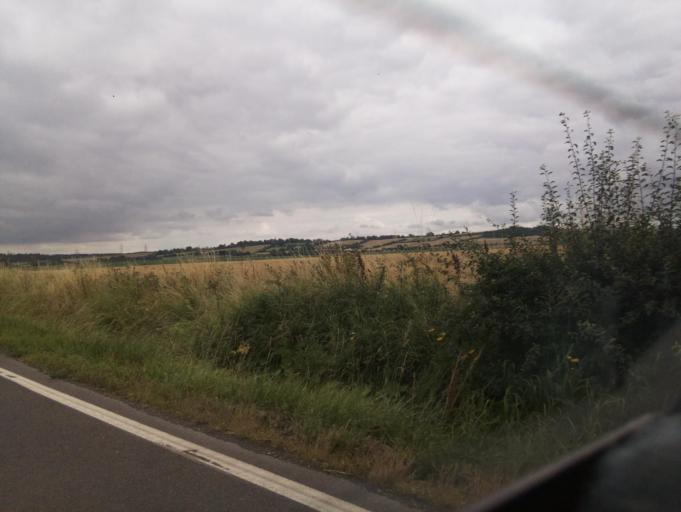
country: GB
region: England
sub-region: Lincolnshire
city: Barrowby
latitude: 52.9300
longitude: -0.7240
